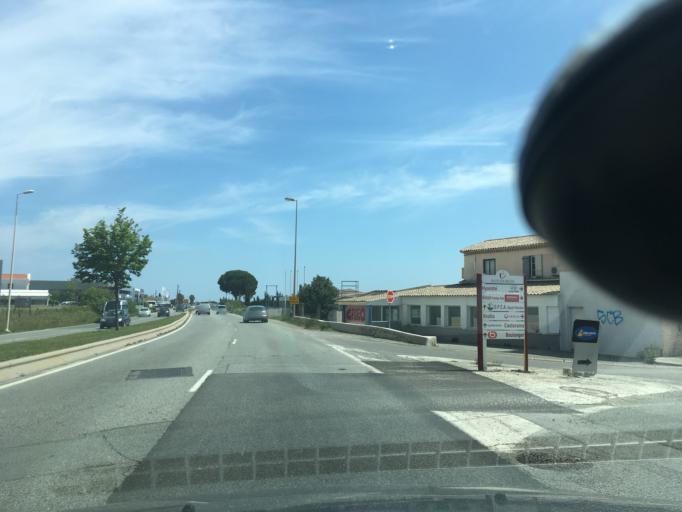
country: FR
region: Provence-Alpes-Cote d'Azur
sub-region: Departement du Var
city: Puget-sur-Argens
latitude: 43.4510
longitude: 6.6924
